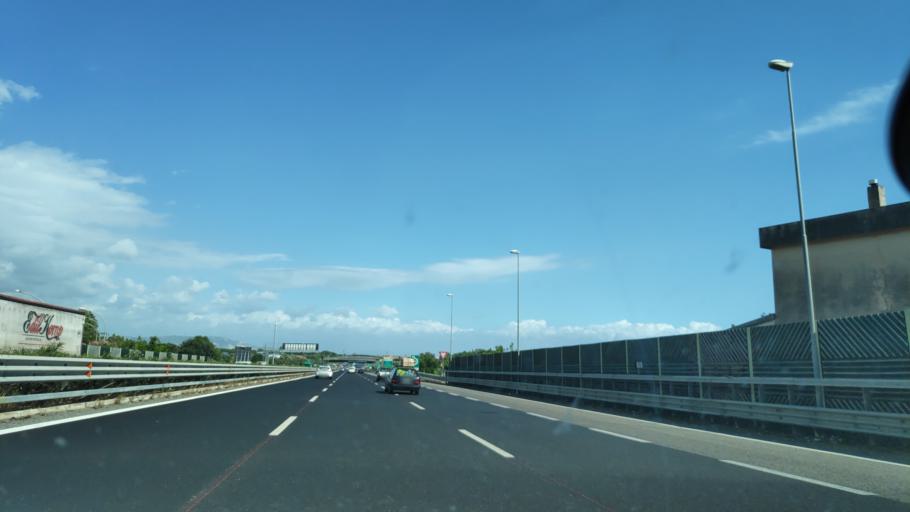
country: IT
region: Campania
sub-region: Provincia di Salerno
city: Pontecagnano
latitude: 40.6549
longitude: 14.8679
